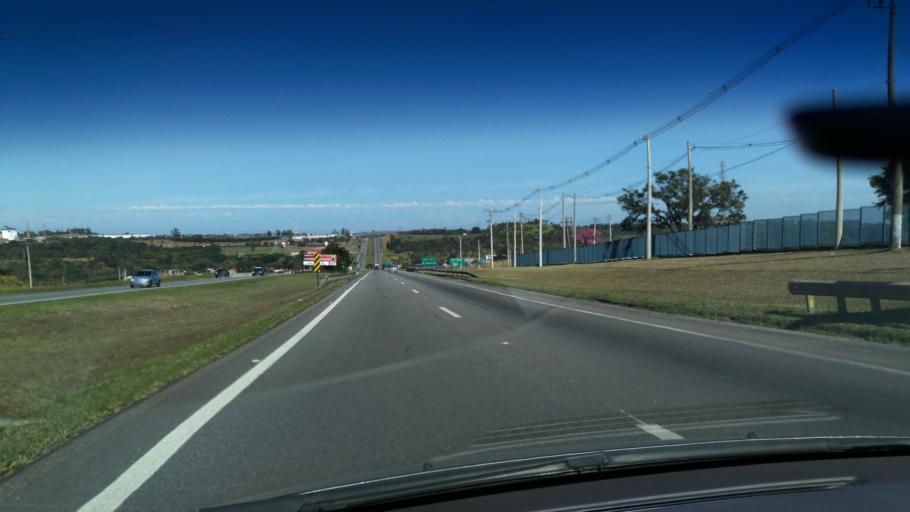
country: BR
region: Sao Paulo
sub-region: Jaguariuna
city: Jaguariuna
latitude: -22.6920
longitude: -47.0127
